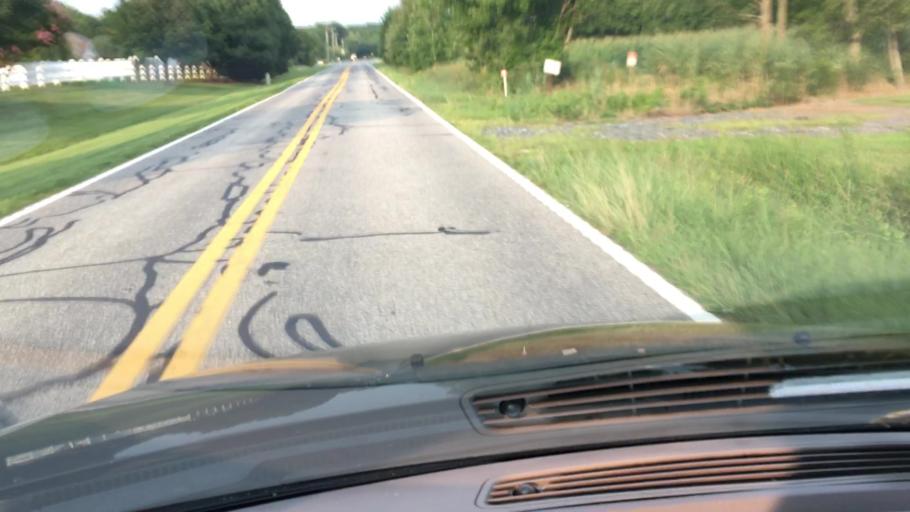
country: US
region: Delaware
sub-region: Sussex County
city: Ocean View
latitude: 38.5183
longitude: -75.0786
